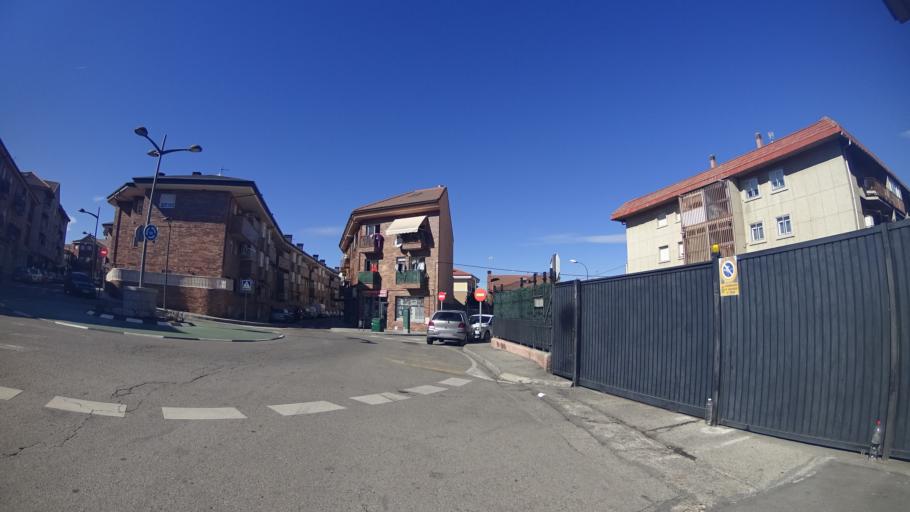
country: ES
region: Madrid
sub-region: Provincia de Madrid
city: Galapagar
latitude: 40.5759
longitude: -4.0006
